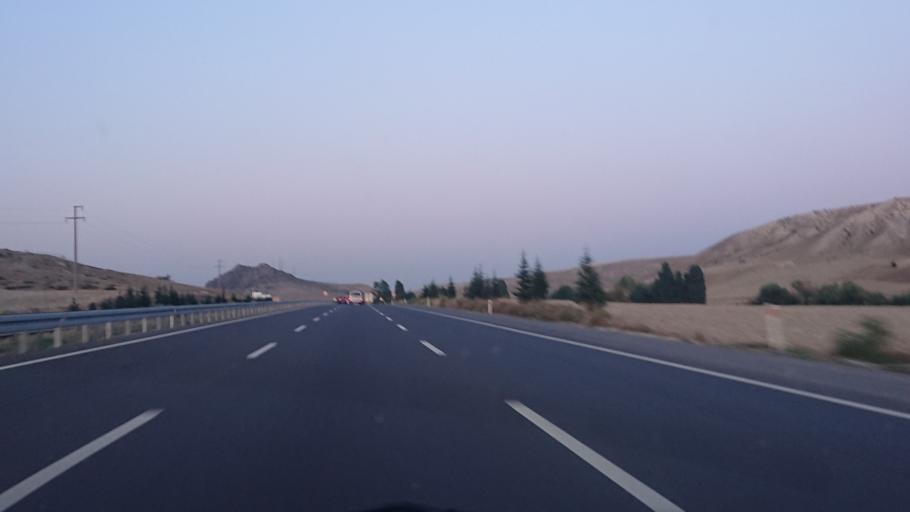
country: TR
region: Ankara
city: Temelli
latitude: 39.7628
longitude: 32.4719
